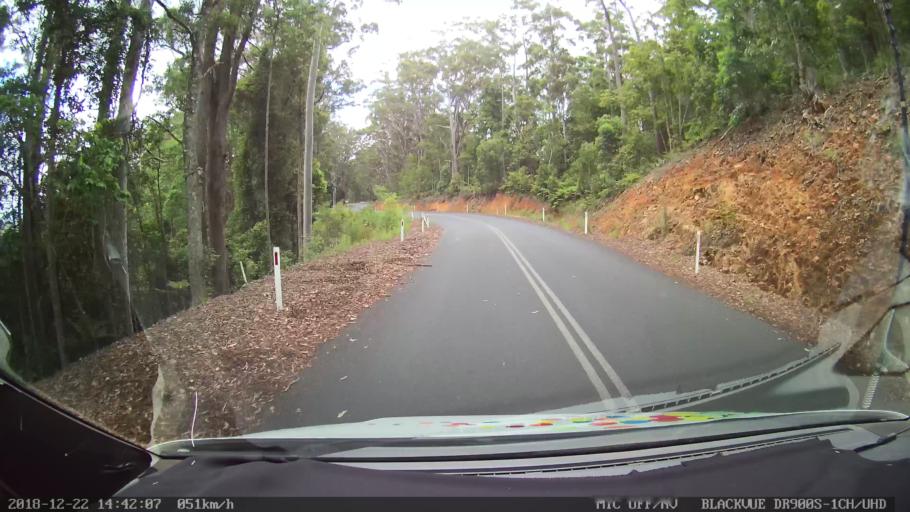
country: AU
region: New South Wales
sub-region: Bellingen
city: Dorrigo
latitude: -30.1571
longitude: 152.5855
